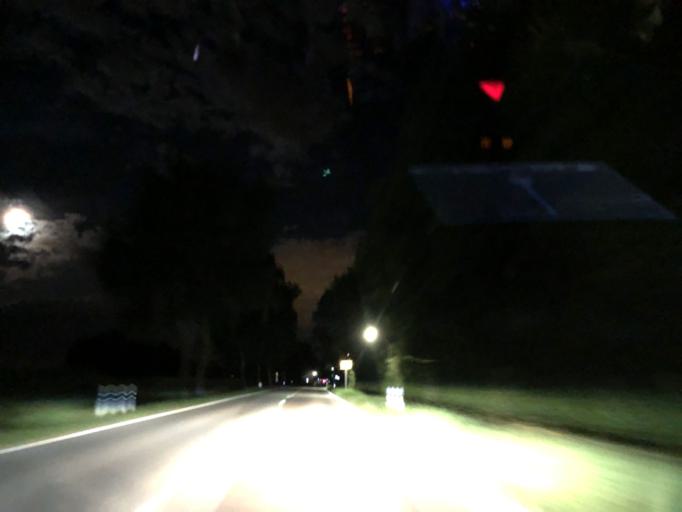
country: DE
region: Bavaria
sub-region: Upper Bavaria
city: Moosinning
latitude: 48.2499
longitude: 11.8392
